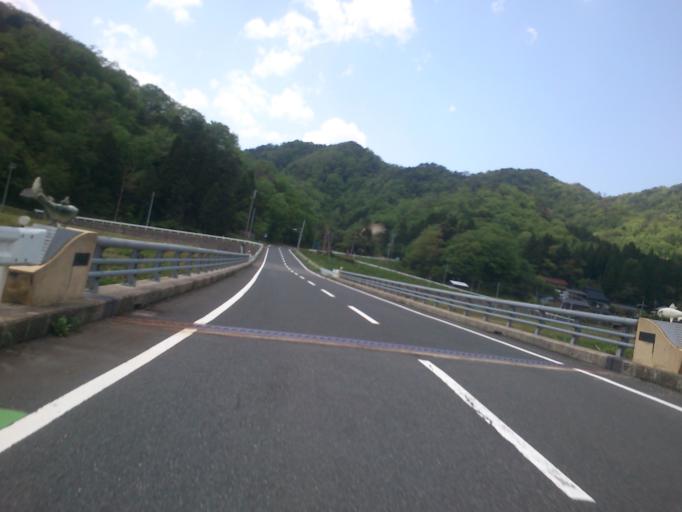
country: JP
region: Kyoto
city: Miyazu
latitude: 35.6923
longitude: 135.1493
